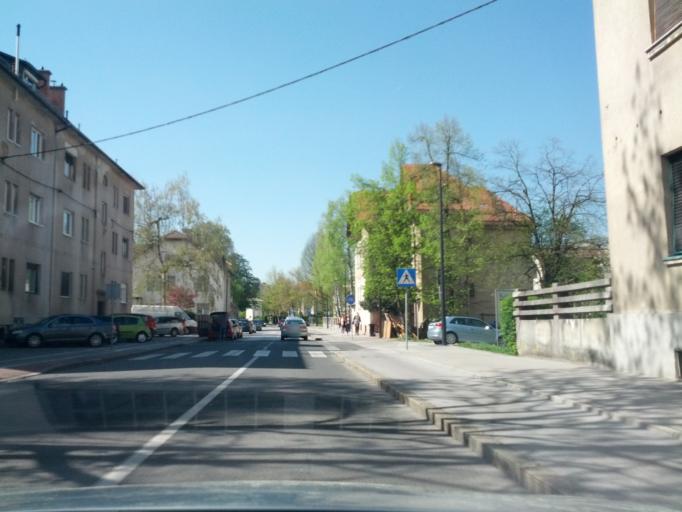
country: SI
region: Ljubljana
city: Ljubljana
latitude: 46.0451
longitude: 14.5163
